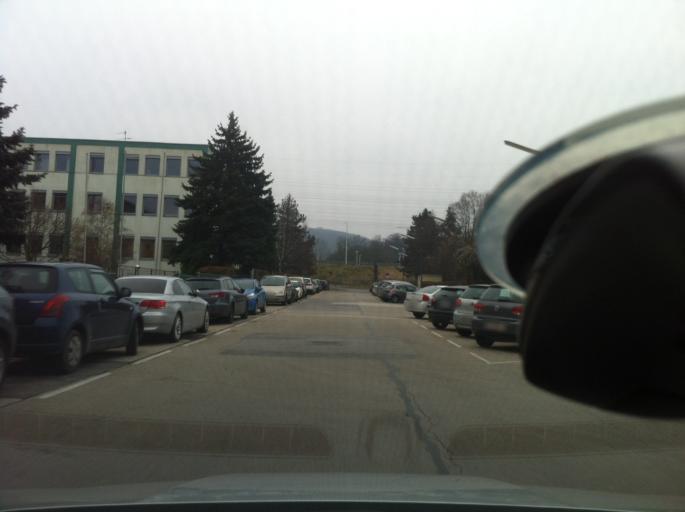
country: AT
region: Lower Austria
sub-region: Politischer Bezirk Wien-Umgebung
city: Purkersdorf
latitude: 48.2056
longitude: 16.2194
